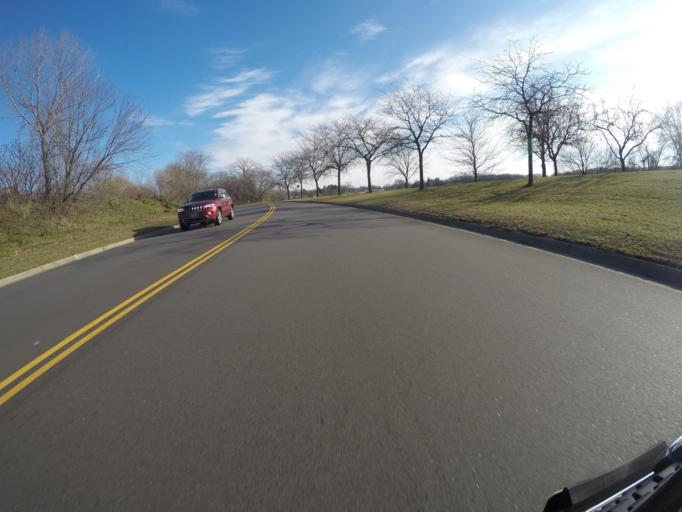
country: US
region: Minnesota
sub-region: Hennepin County
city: Eden Prairie
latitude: 44.8706
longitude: -93.4947
